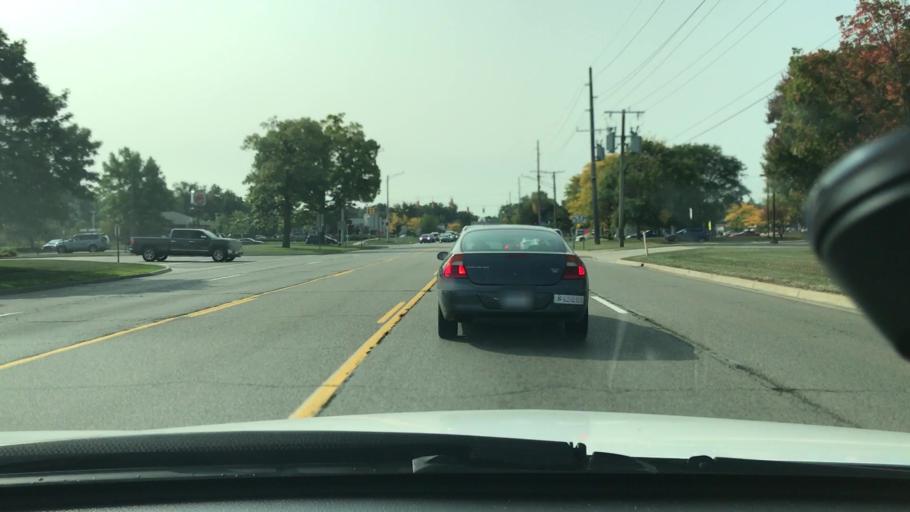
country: US
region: Michigan
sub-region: Oakland County
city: Wolverine Lake
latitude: 42.5937
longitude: -83.4461
